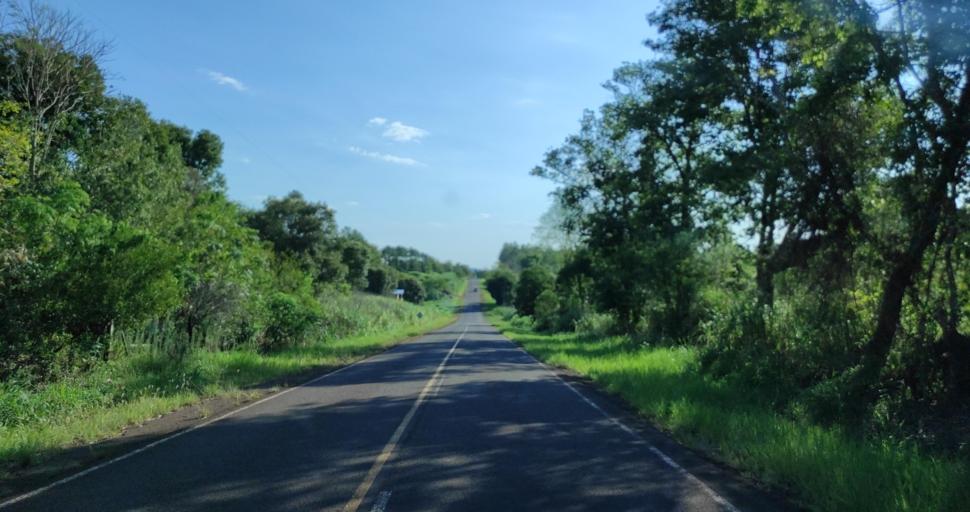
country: AR
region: Misiones
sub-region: Departamento de Eldorado
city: Eldorado
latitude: -26.3796
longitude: -54.3385
